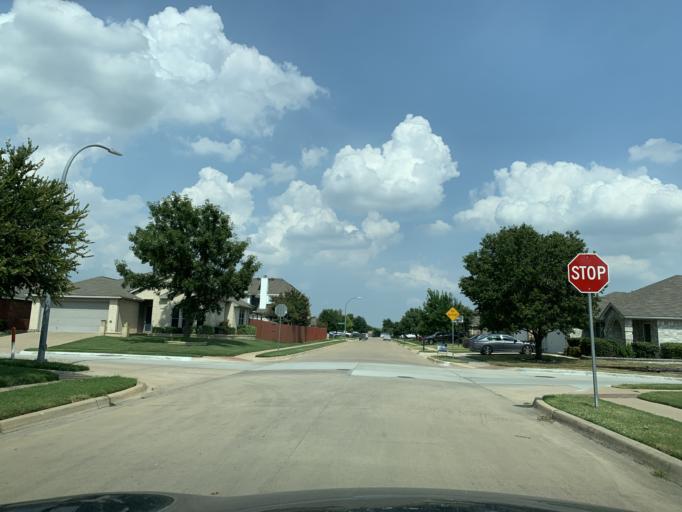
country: US
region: Texas
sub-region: Tarrant County
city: Richland Hills
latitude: 32.8032
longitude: -97.1979
